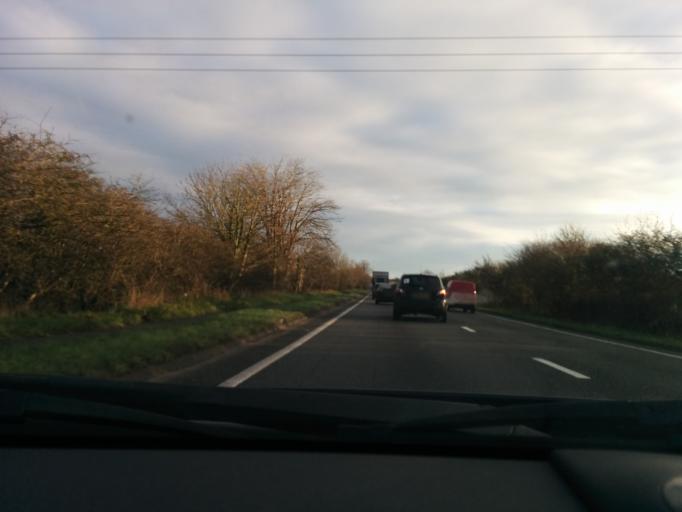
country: GB
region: England
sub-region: Oxfordshire
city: Oxford
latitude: 51.7403
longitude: -1.2777
